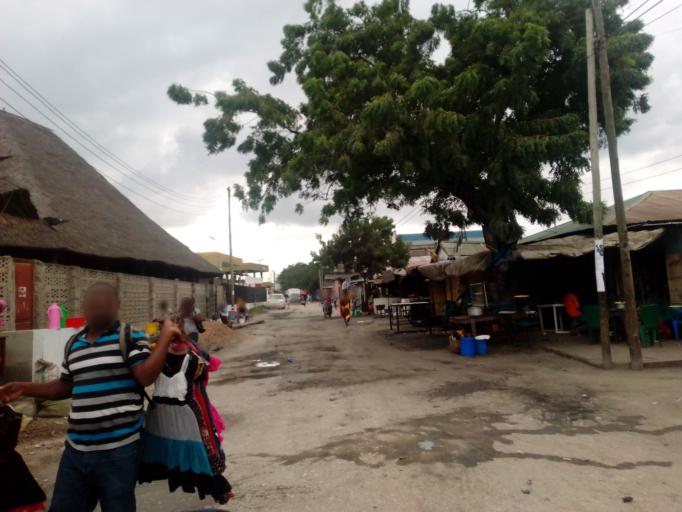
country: TZ
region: Dar es Salaam
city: Dar es Salaam
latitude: -6.8420
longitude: 39.2741
